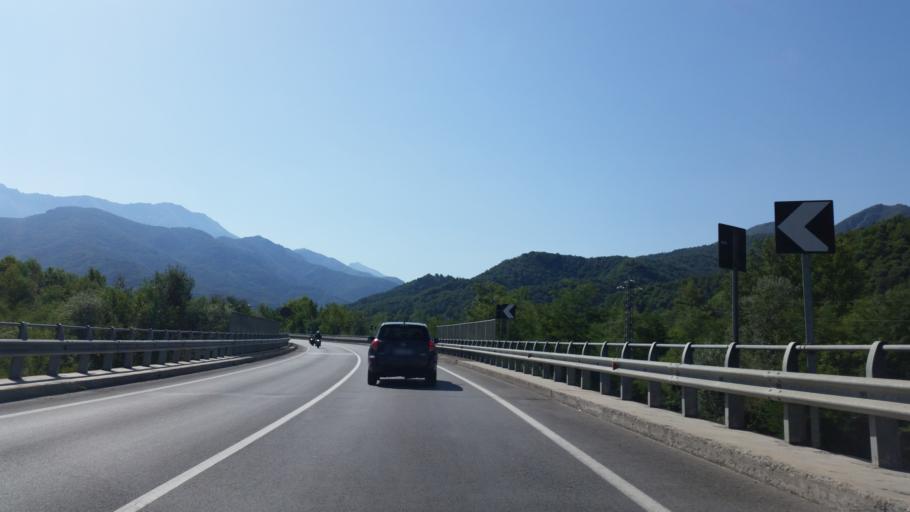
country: IT
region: Piedmont
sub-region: Provincia di Cuneo
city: Roccavione
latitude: 44.3148
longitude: 7.4882
